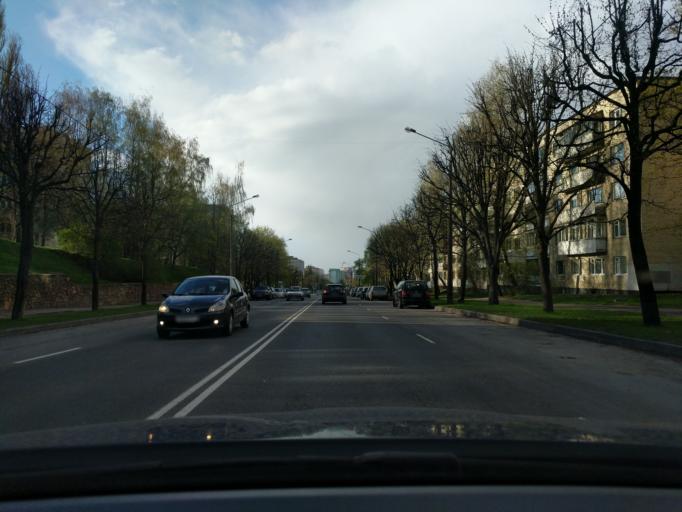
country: BY
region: Minsk
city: Novoye Medvezhino
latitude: 53.9130
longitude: 27.4802
